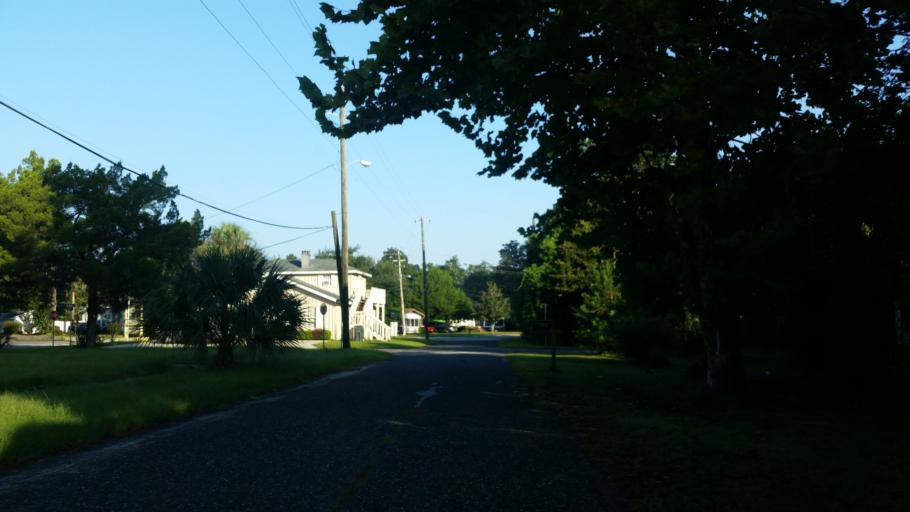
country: US
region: Florida
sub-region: Santa Rosa County
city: Milton
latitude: 30.6232
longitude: -87.0385
